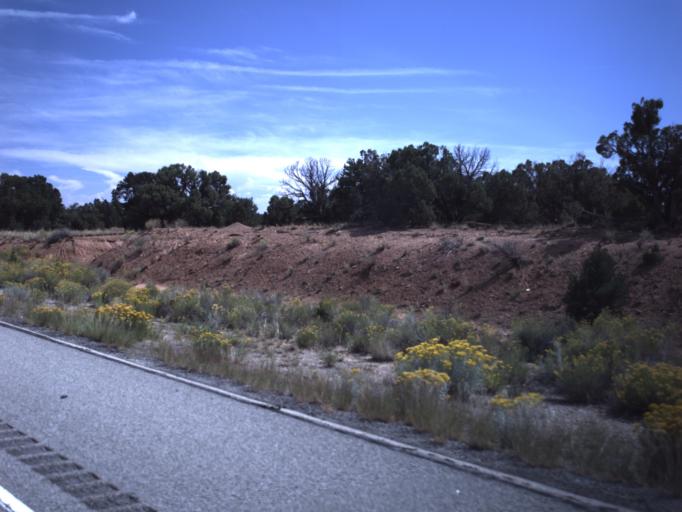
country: US
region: Utah
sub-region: Emery County
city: Castle Dale
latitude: 38.8698
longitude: -110.7245
